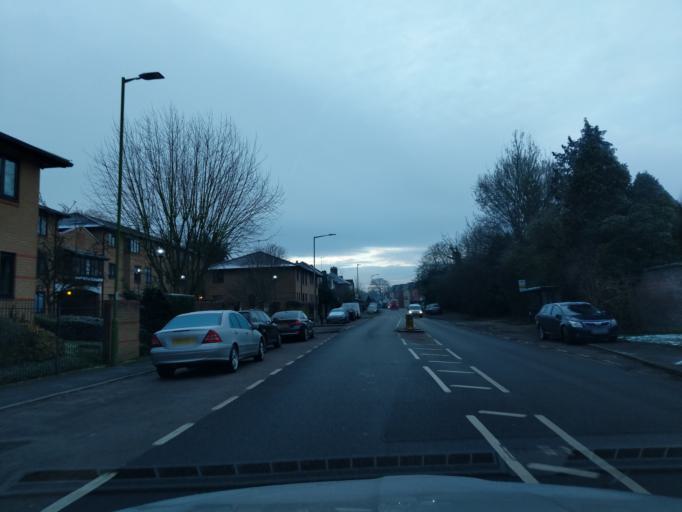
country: GB
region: England
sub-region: Hertfordshire
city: Kings Langley
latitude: 51.7197
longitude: -0.4452
